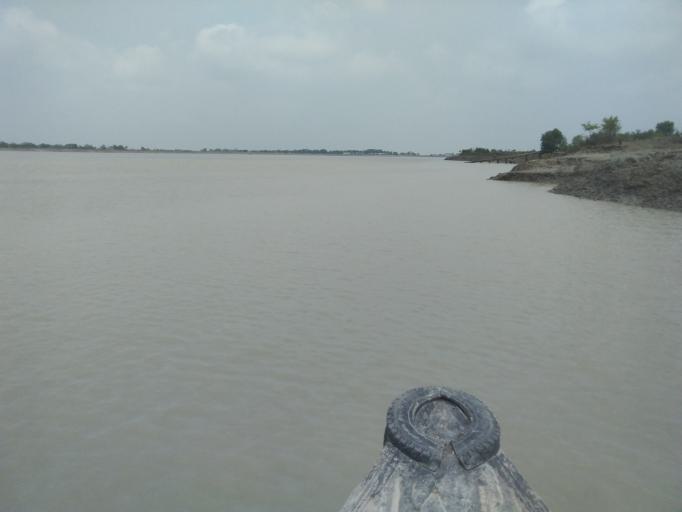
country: BD
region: Khulna
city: Phultala
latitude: 22.6465
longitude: 89.4102
